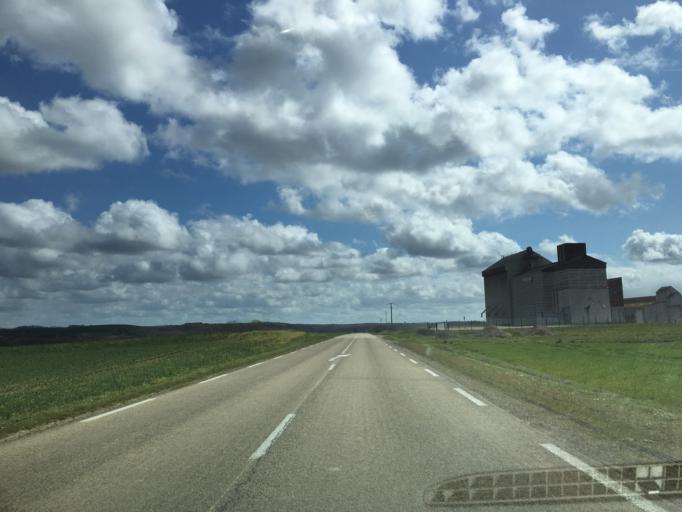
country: FR
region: Bourgogne
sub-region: Departement de l'Yonne
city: Aillant-sur-Tholon
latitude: 47.8515
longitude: 3.3789
